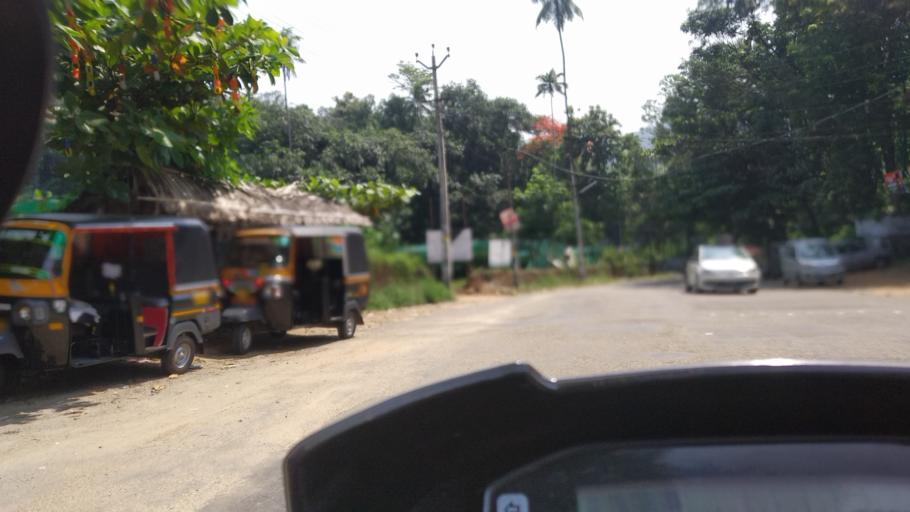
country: IN
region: Kerala
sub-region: Kottayam
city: Erattupetta
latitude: 9.6994
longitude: 76.8054
